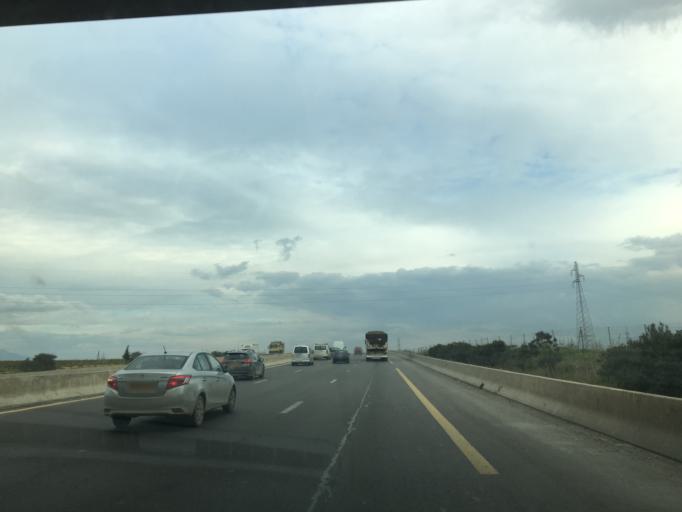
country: DZ
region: Bouira
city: Bouira
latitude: 36.3291
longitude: 3.9507
